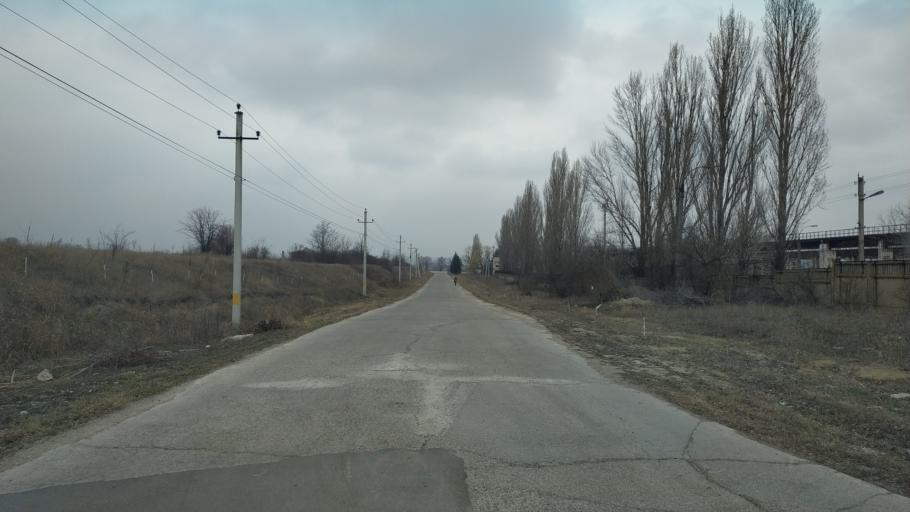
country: MD
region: Chisinau
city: Singera
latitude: 46.9101
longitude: 29.0070
